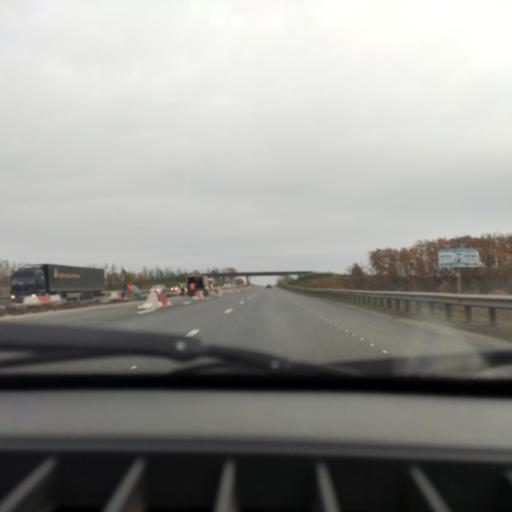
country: RU
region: Bashkortostan
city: Avdon
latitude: 54.6669
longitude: 55.7513
